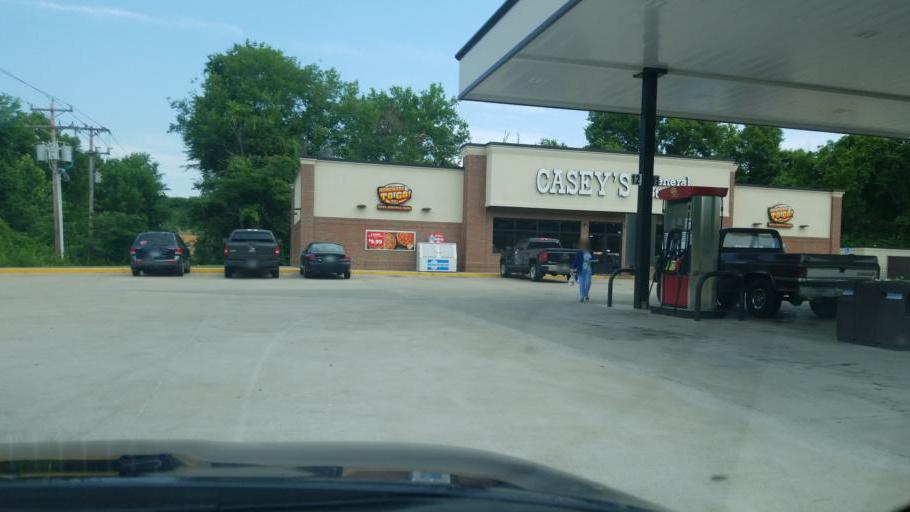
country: US
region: Tennessee
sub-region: Humphreys County
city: Waverly
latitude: 36.0842
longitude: -87.8039
